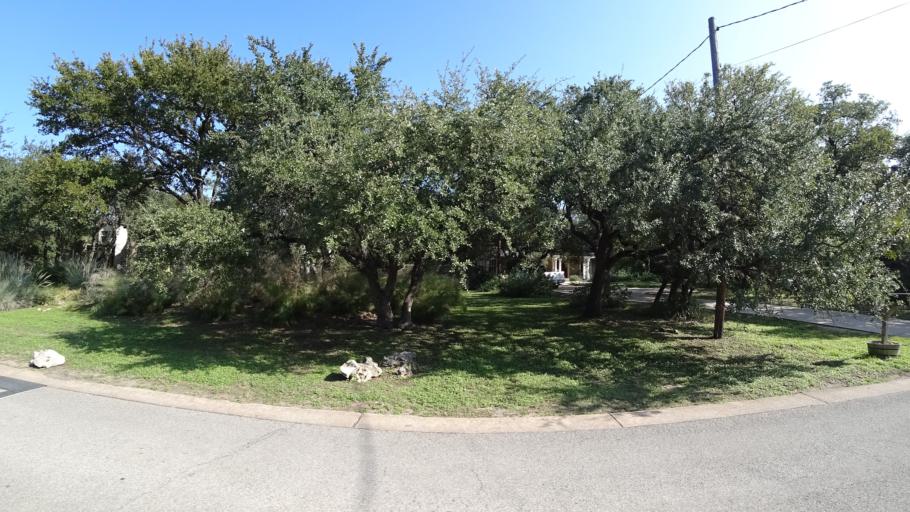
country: US
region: Texas
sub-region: Travis County
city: West Lake Hills
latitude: 30.2871
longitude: -97.8007
